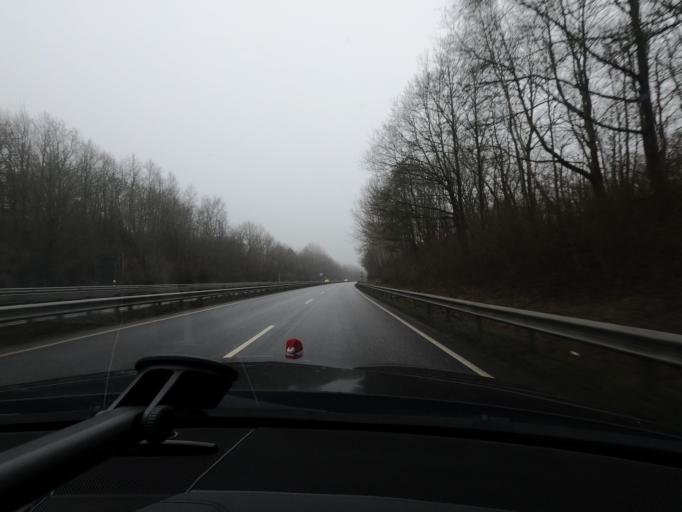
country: DE
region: Schleswig-Holstein
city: Jarplund-Weding
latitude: 54.7538
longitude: 9.4295
